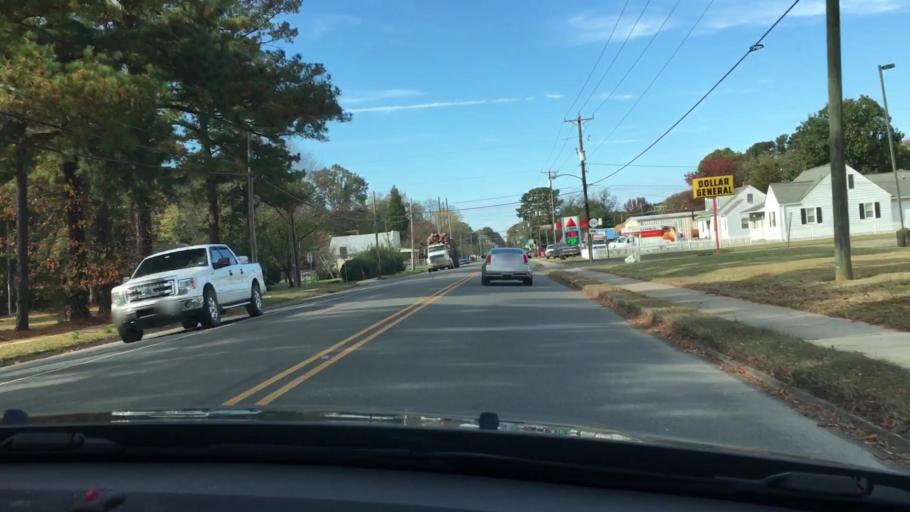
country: US
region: Virginia
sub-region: King William County
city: West Point
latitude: 37.5507
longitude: -76.8095
